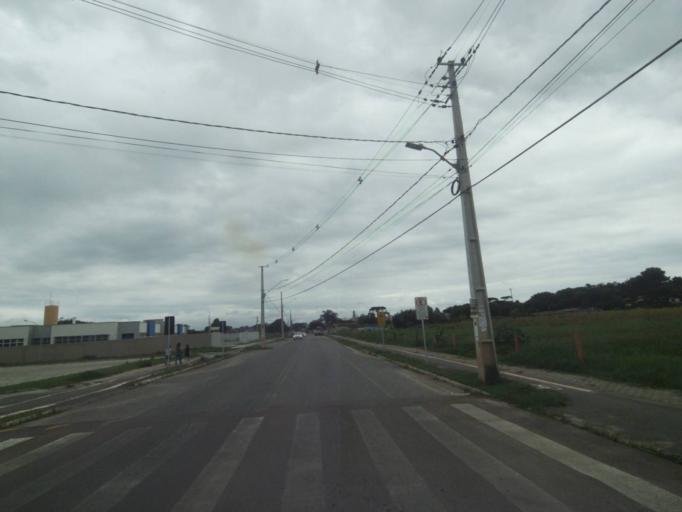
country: BR
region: Parana
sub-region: Quatro Barras
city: Quatro Barras
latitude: -25.3576
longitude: -49.1032
